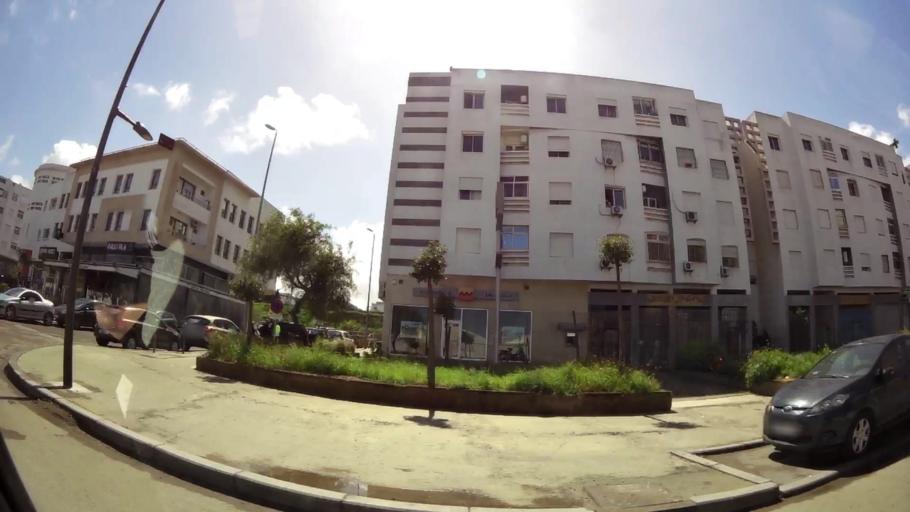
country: MA
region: Grand Casablanca
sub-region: Mediouna
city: Tit Mellil
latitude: 33.6079
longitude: -7.5233
